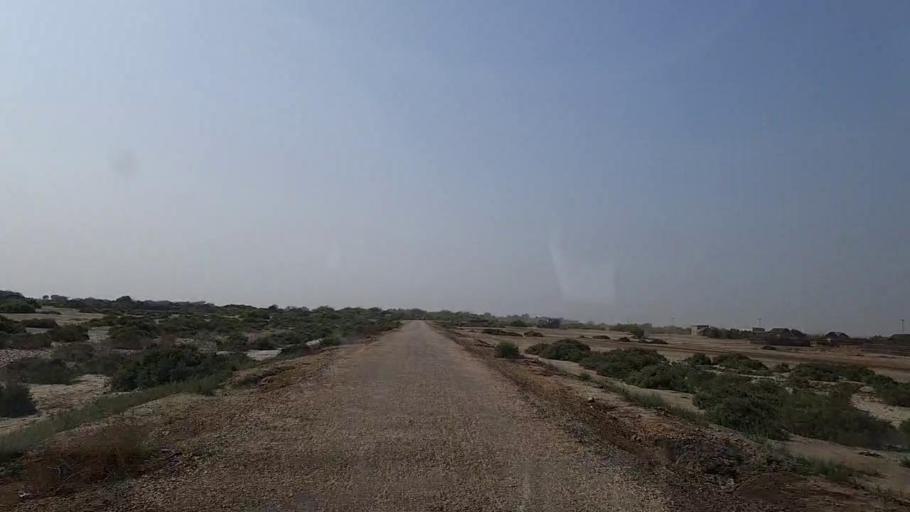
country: PK
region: Sindh
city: Mirpur Sakro
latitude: 24.5286
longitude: 67.5654
